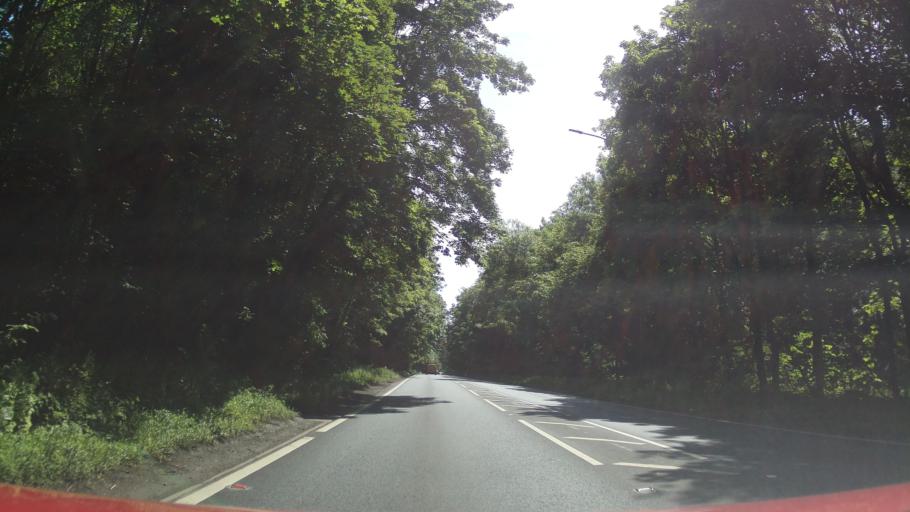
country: GB
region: England
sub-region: North Lincolnshire
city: Broughton
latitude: 53.5514
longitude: -0.5695
